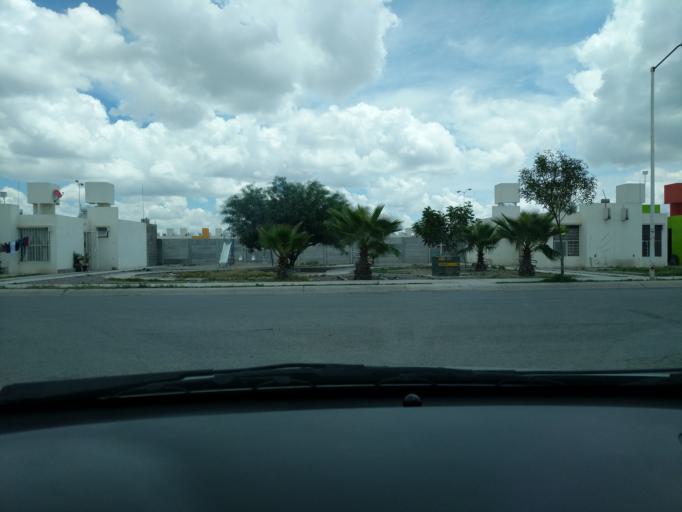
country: MX
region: San Luis Potosi
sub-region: San Luis Potosi
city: Fraccion Milpillas
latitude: 22.2182
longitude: -100.9344
